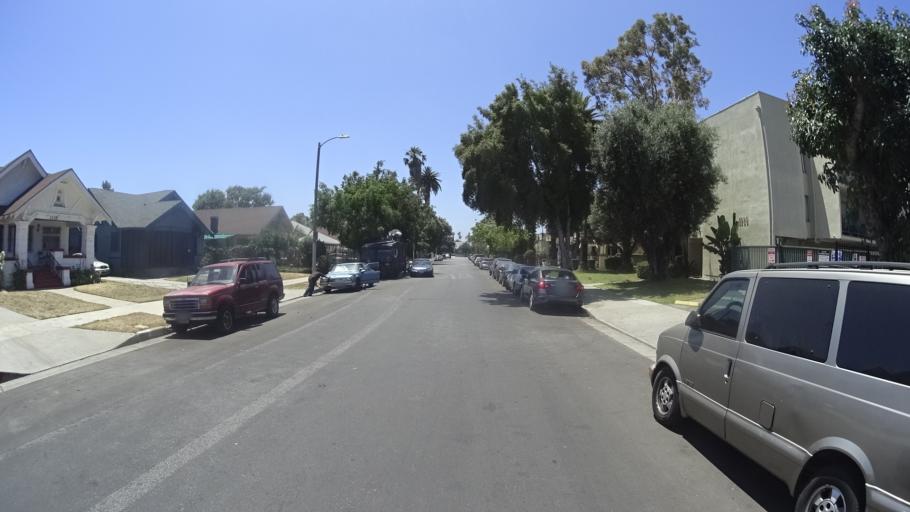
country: US
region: California
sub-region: Los Angeles County
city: View Park-Windsor Hills
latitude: 34.0142
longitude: -118.2978
